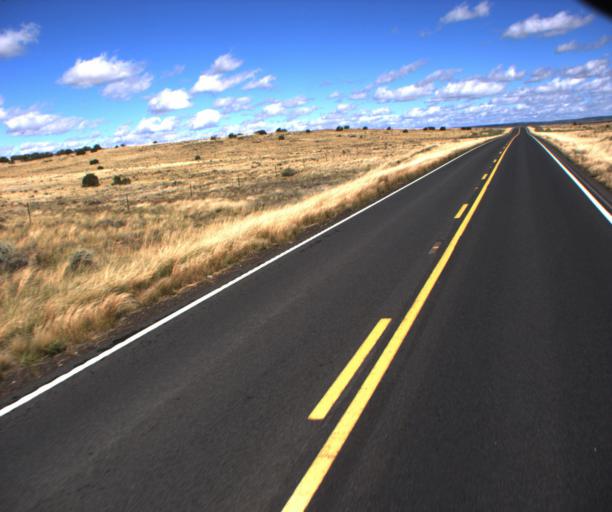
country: US
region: Arizona
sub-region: Apache County
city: Houck
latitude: 34.9696
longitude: -109.2273
